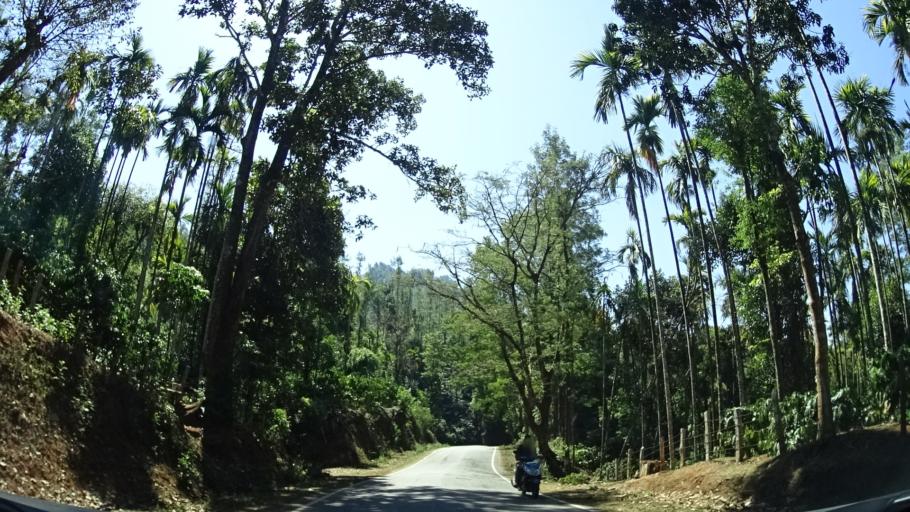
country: IN
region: Karnataka
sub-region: Chikmagalur
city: Sringeri
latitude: 13.2024
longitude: 75.3360
